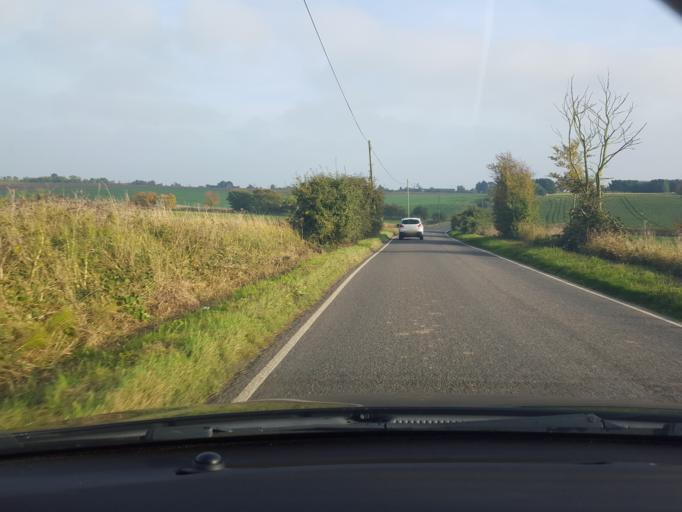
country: GB
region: England
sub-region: Essex
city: Frinton-on-Sea
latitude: 51.8602
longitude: 1.1952
